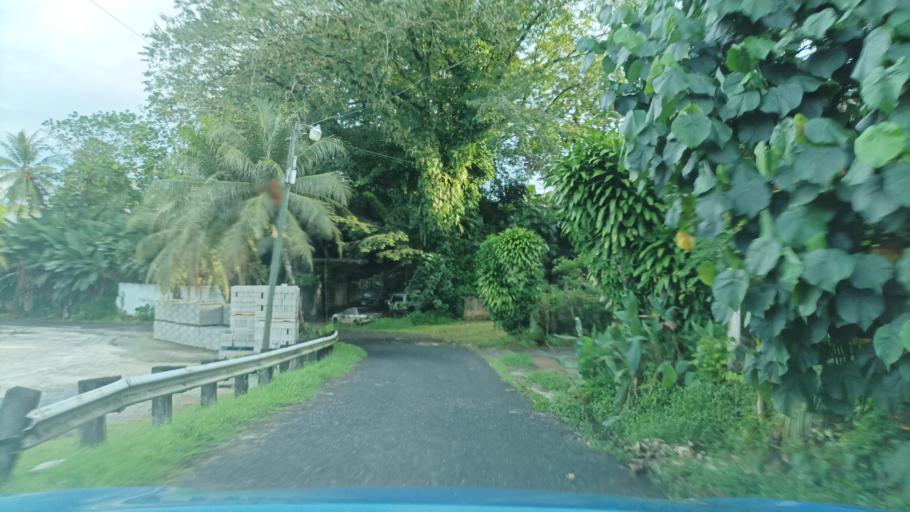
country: FM
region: Pohnpei
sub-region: Kolonia Municipality
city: Kolonia
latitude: 6.9657
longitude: 158.2122
